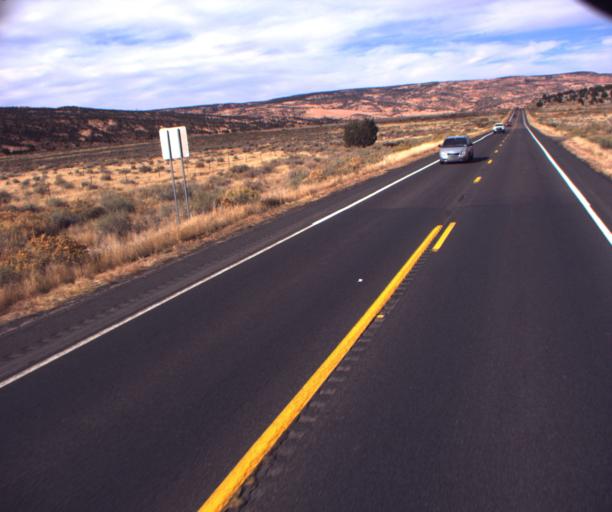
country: US
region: Arizona
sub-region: Navajo County
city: Kayenta
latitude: 36.5866
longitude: -110.4718
